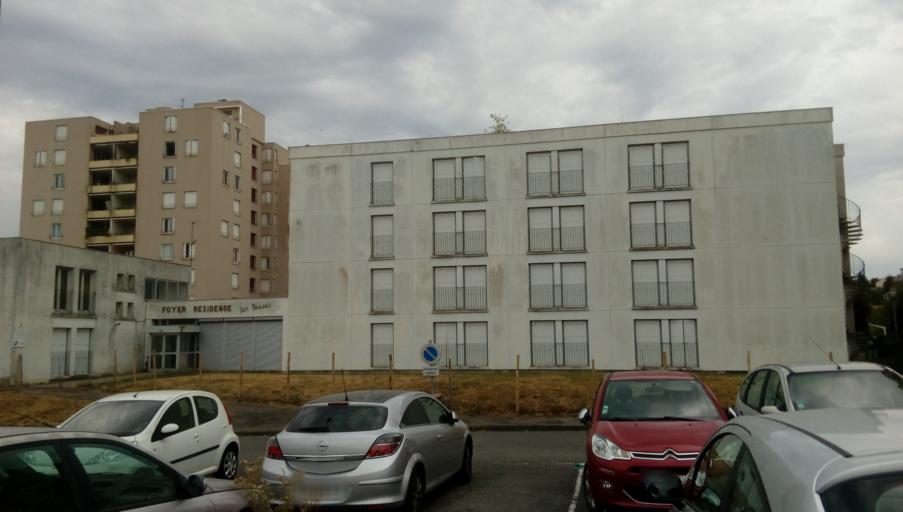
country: FR
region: Limousin
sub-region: Departement de la Creuse
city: Gueret
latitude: 46.1763
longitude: 1.8702
